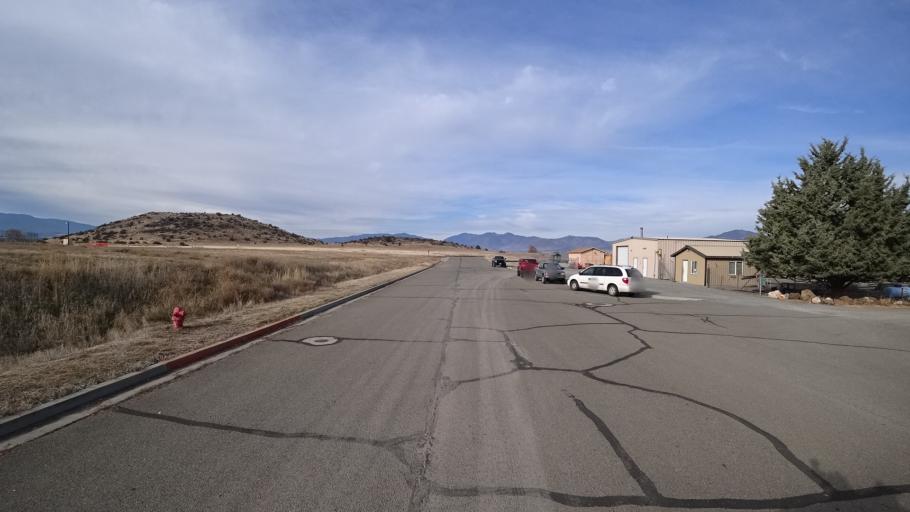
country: US
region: California
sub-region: Siskiyou County
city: Montague
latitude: 41.7310
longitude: -122.5352
